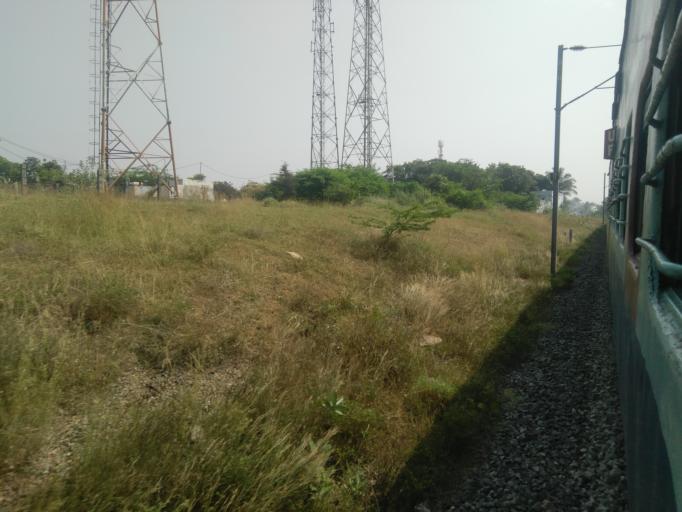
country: IN
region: Tamil Nadu
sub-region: Coimbatore
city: Karamadai
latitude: 11.2624
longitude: 76.9504
